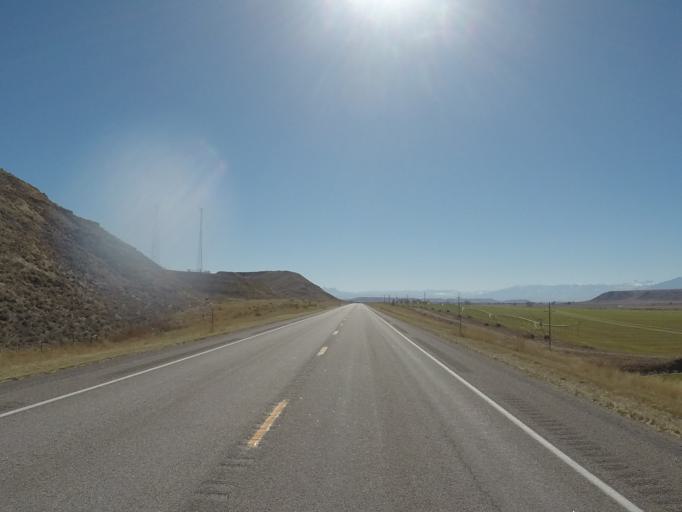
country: US
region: Montana
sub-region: Carbon County
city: Red Lodge
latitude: 45.0449
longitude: -109.0537
